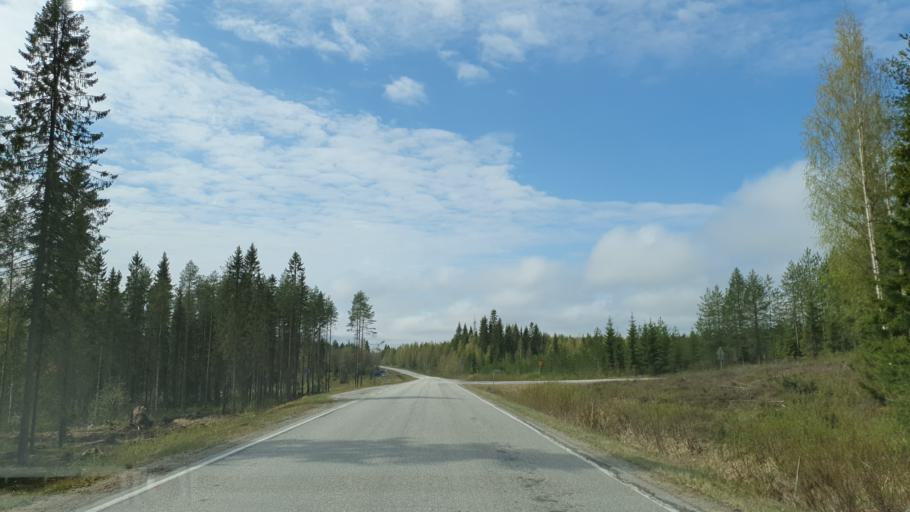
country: FI
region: Kainuu
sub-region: Kehys-Kainuu
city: Kuhmo
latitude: 64.1253
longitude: 29.6413
